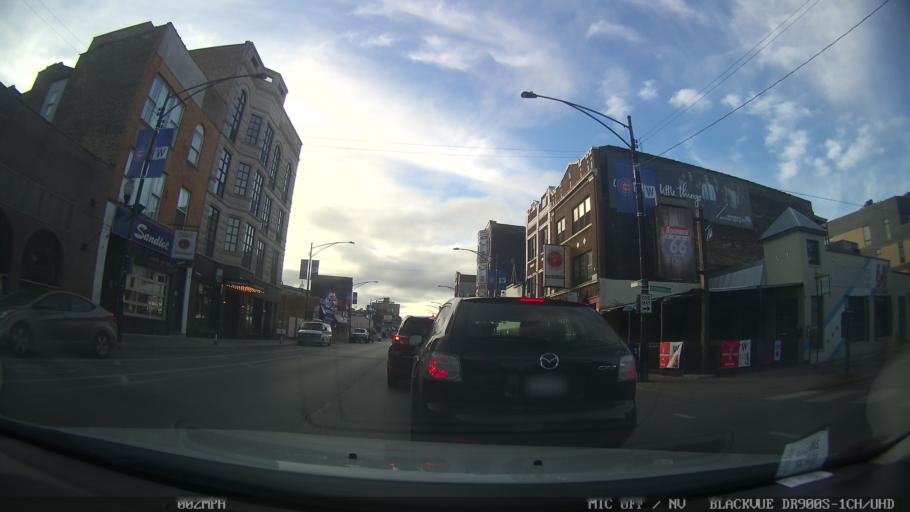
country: US
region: Illinois
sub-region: Cook County
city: Lincolnwood
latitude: 41.9456
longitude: -87.6552
